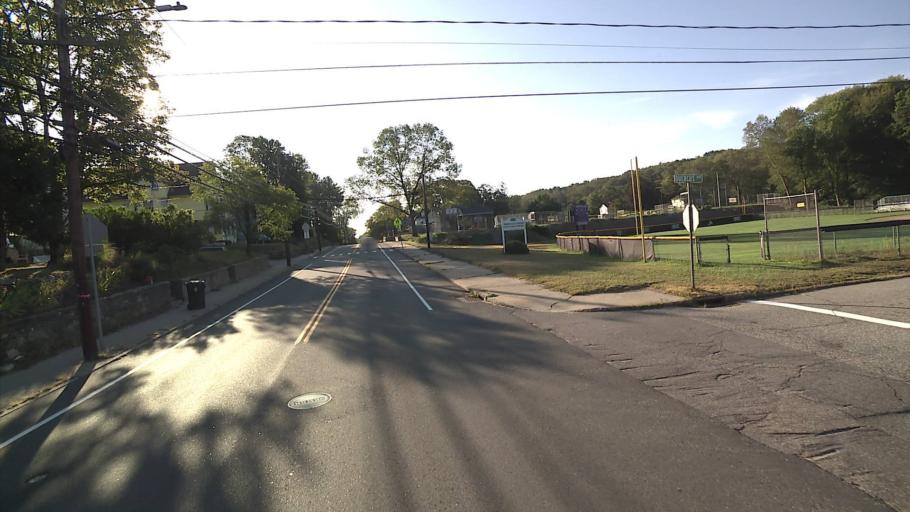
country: US
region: Connecticut
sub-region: Windham County
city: Willimantic
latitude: 41.7076
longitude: -72.2024
